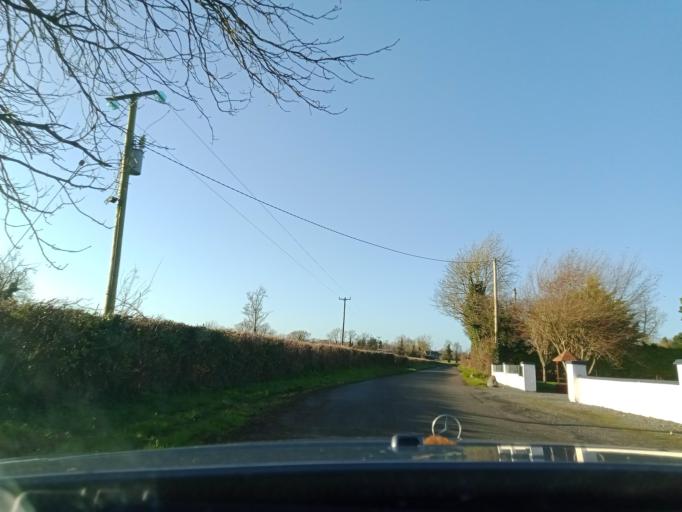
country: IE
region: Leinster
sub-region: Kilkenny
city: Callan
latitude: 52.5011
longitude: -7.3653
